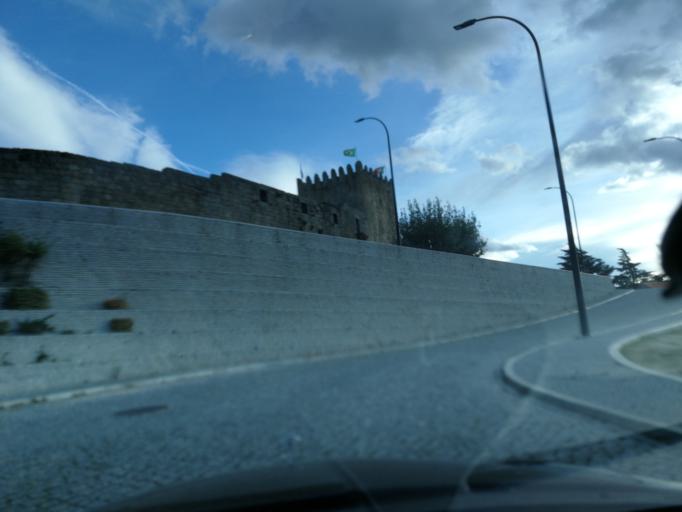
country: PT
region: Castelo Branco
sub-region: Belmonte
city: Belmonte
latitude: 40.3599
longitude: -7.3482
